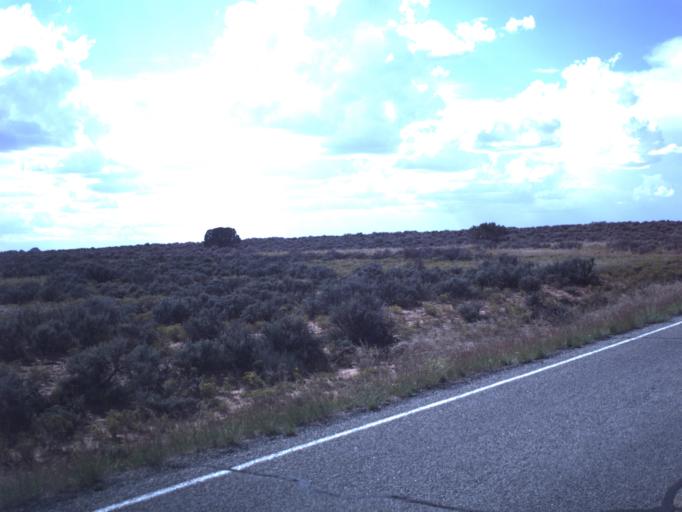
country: US
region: Utah
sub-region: Grand County
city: Moab
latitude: 38.5254
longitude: -109.7450
